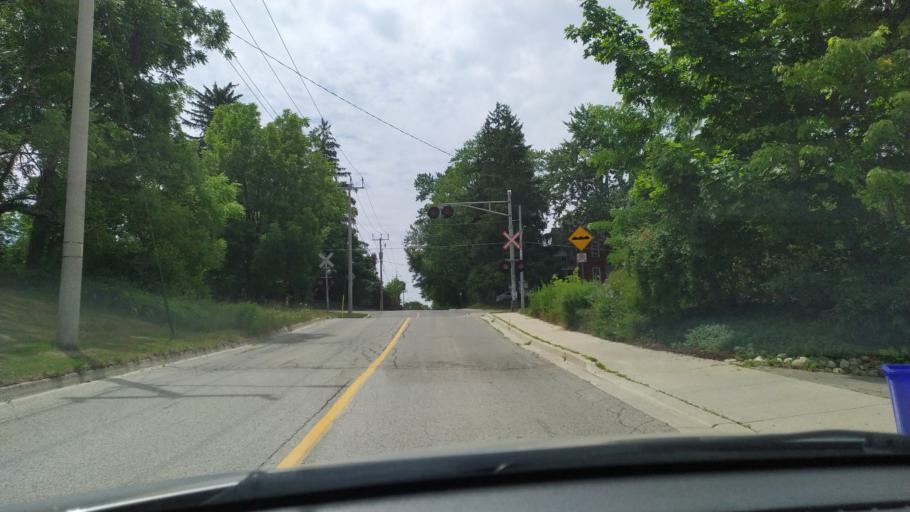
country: CA
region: Ontario
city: Stratford
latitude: 43.3705
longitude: -80.9913
